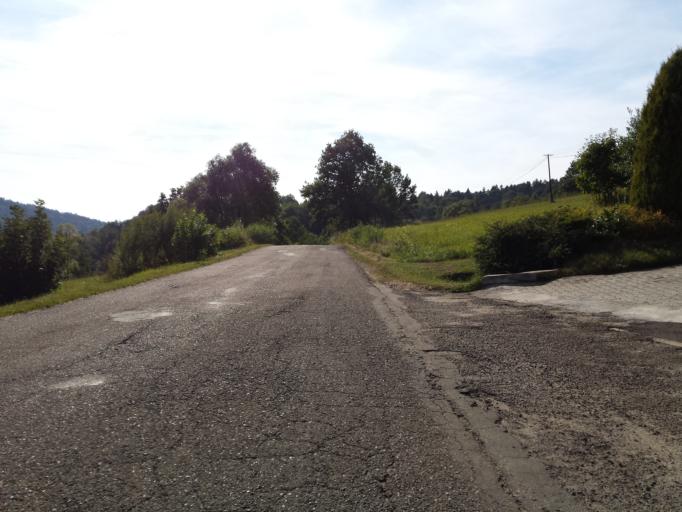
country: PL
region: Subcarpathian Voivodeship
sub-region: Powiat leski
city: Olszanica
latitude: 49.5123
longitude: 22.4822
